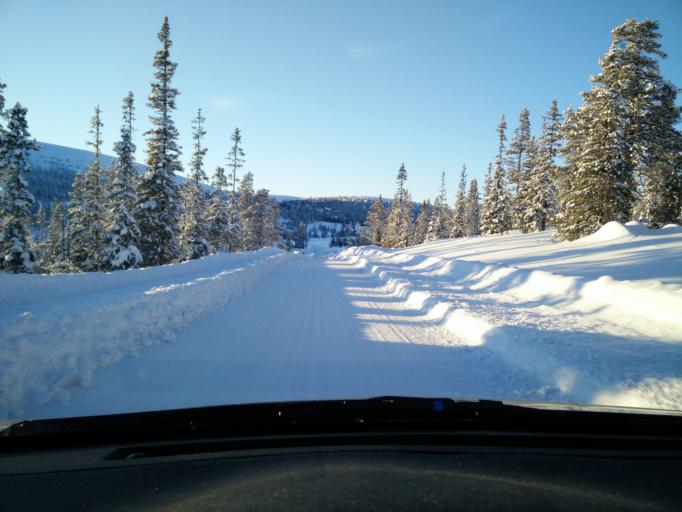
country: SE
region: Jaemtland
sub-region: Bergs Kommun
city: Hoverberg
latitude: 62.4966
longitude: 14.1208
